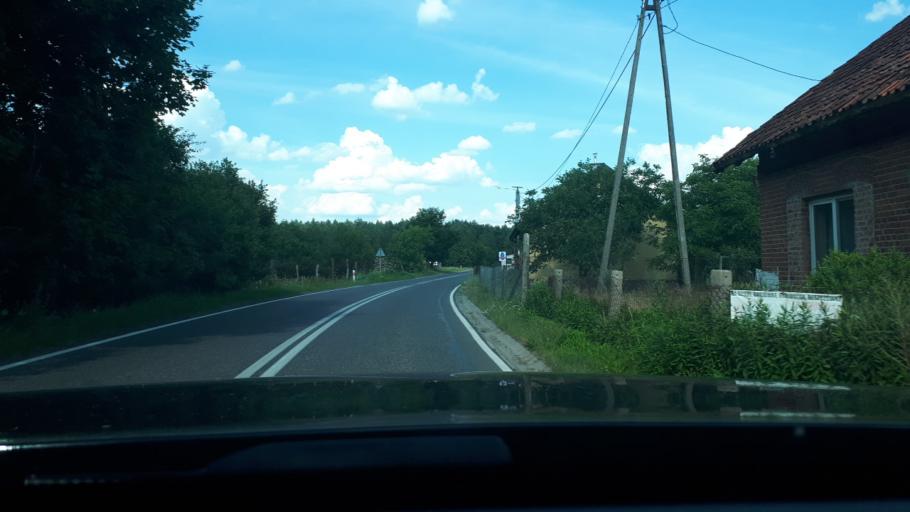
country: PL
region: Warmian-Masurian Voivodeship
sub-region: Powiat olsztynski
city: Stawiguda
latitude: 53.5279
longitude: 20.4486
